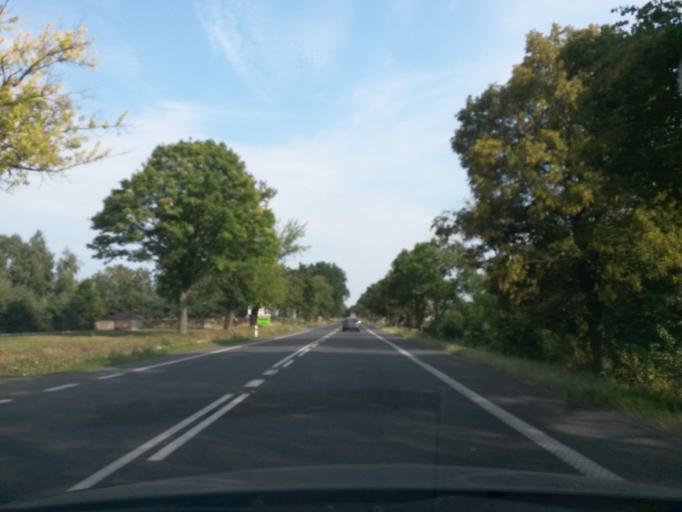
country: PL
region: Masovian Voivodeship
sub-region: Powiat sierpecki
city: Sierpc
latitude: 52.8494
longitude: 19.7072
